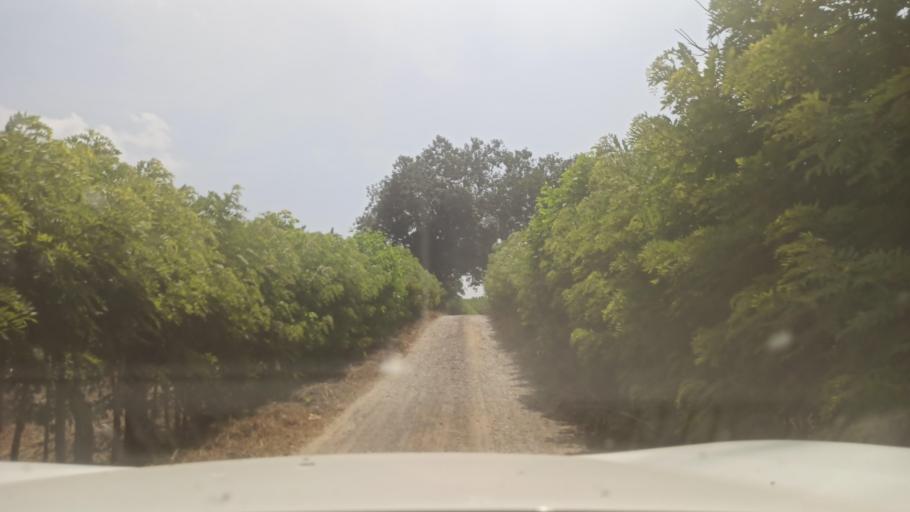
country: MX
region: Veracruz
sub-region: Atzalan
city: Colonias Pedernales
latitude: 20.0396
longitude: -97.0053
